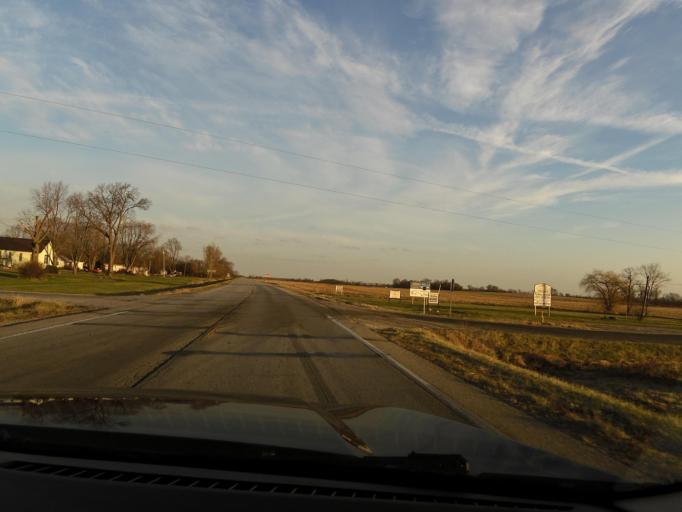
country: US
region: Illinois
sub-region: Fayette County
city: Vandalia
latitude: 38.8670
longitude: -89.0857
